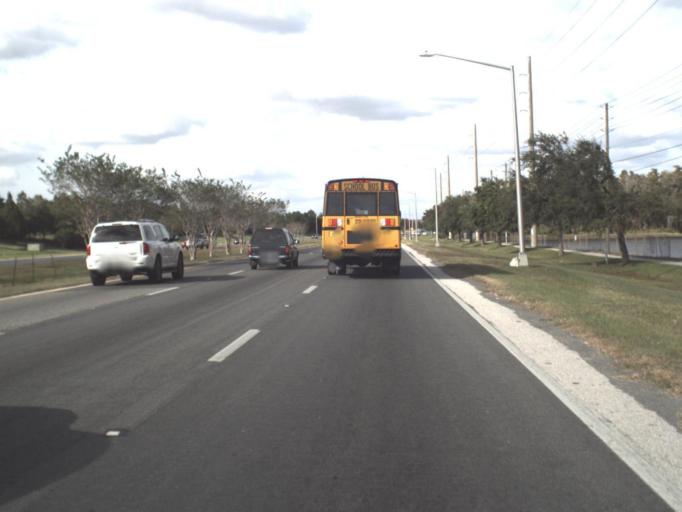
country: US
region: Florida
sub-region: Orange County
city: Williamsburg
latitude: 28.4040
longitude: -81.4250
